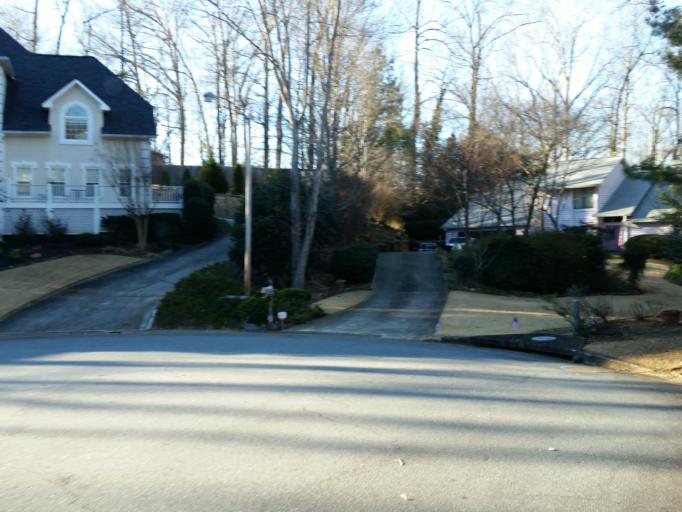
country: US
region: Georgia
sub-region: Cherokee County
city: Woodstock
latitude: 34.0551
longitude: -84.4799
